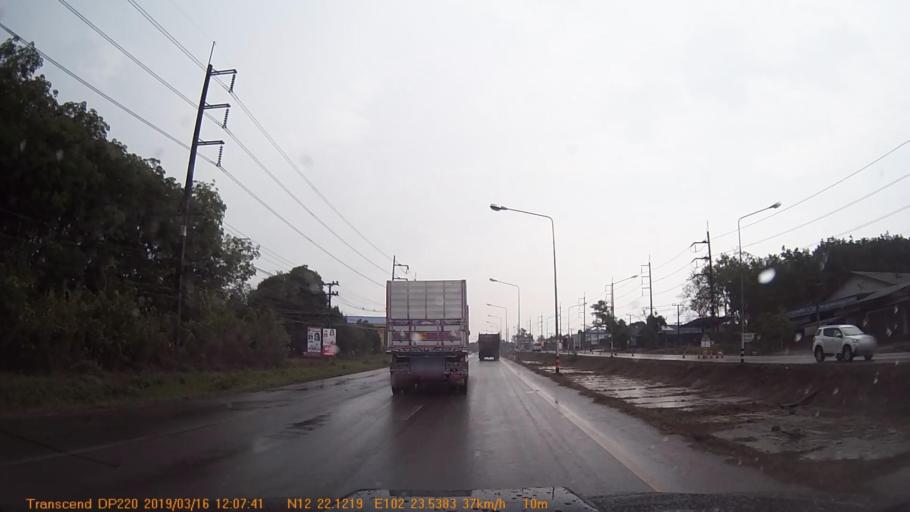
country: TH
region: Trat
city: Khao Saming
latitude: 12.3668
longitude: 102.4028
